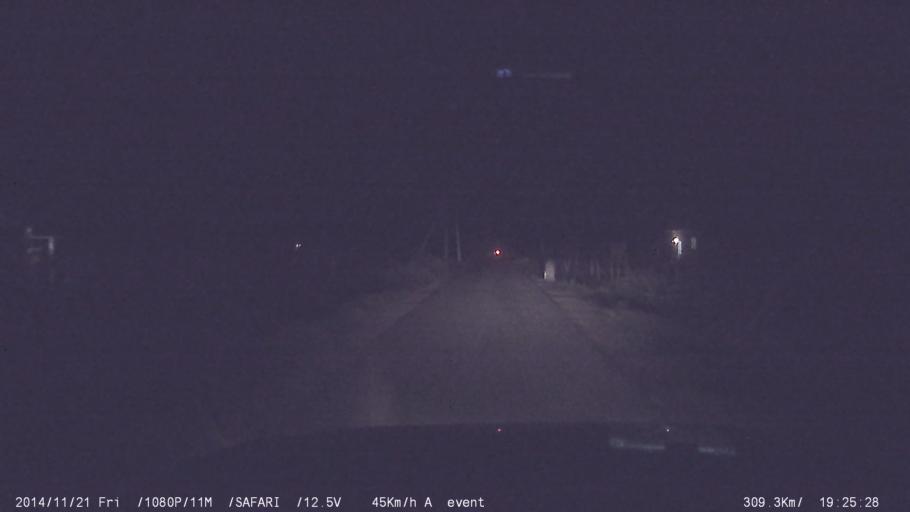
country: IN
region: Tamil Nadu
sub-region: Kancheepuram
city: Singapperumalkovil
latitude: 12.7991
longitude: 79.9826
